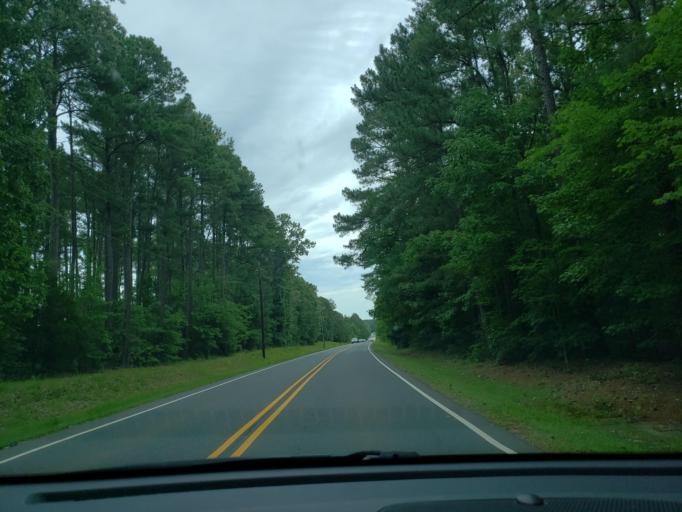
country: US
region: North Carolina
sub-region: Orange County
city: Chapel Hill
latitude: 35.8569
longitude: -79.0149
